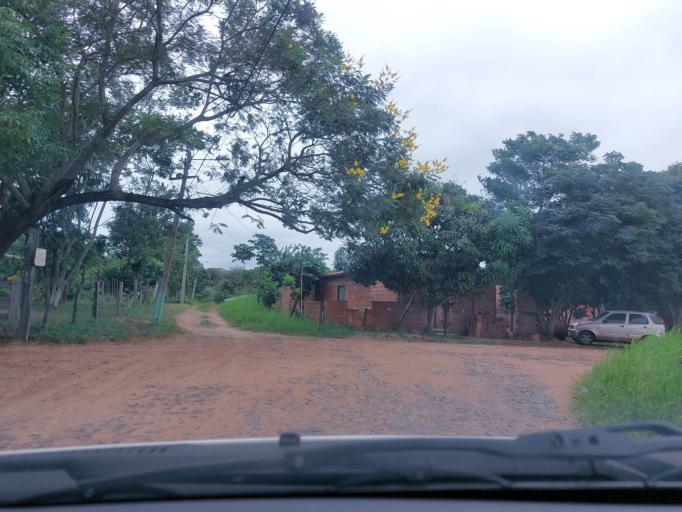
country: PY
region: San Pedro
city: Guayaybi
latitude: -24.6682
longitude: -56.4336
